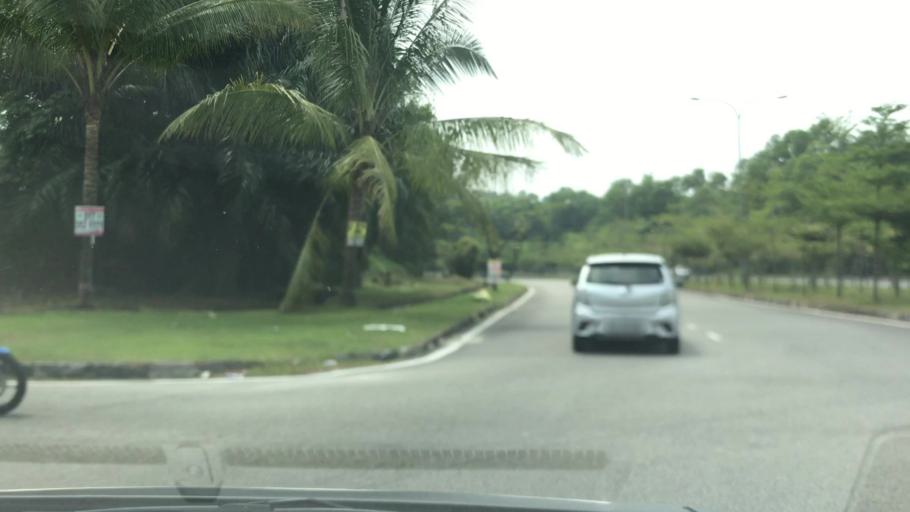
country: MY
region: Putrajaya
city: Putrajaya
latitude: 3.0051
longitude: 101.6658
